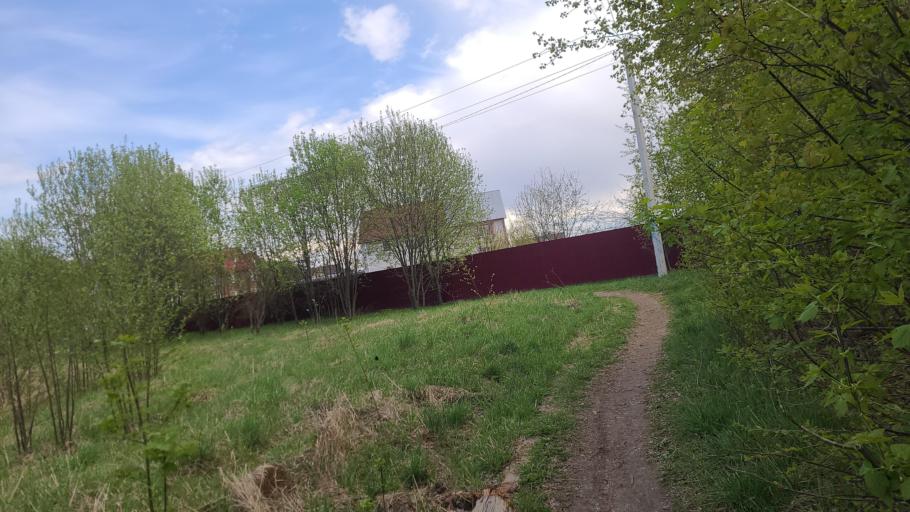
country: RU
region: Moskovskaya
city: Gzhel'
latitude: 55.6107
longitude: 38.4172
